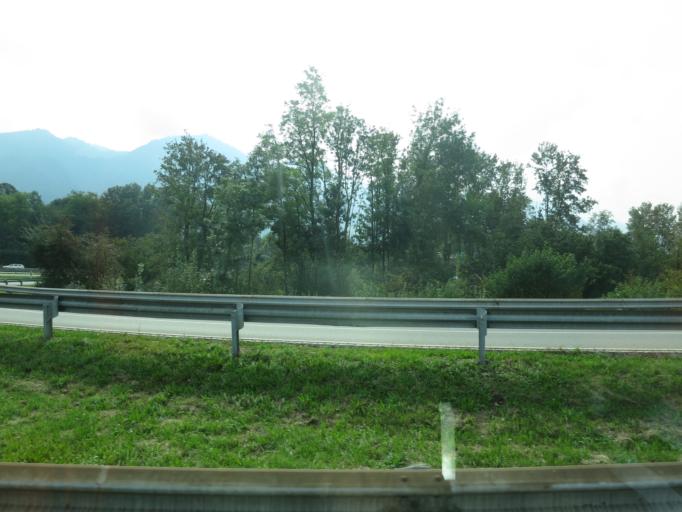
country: CH
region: Schwyz
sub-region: Bezirk March
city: Reichenburg
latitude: 47.1849
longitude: 8.9785
